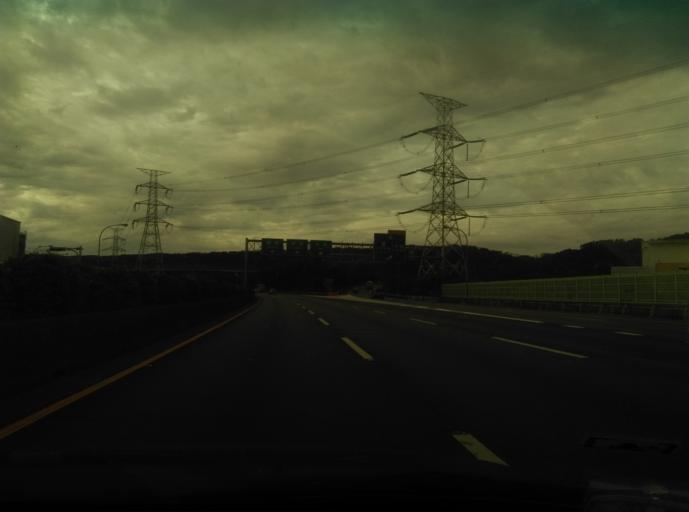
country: TW
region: Taiwan
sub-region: Taoyuan
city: Taoyuan
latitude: 24.9395
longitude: 121.3301
